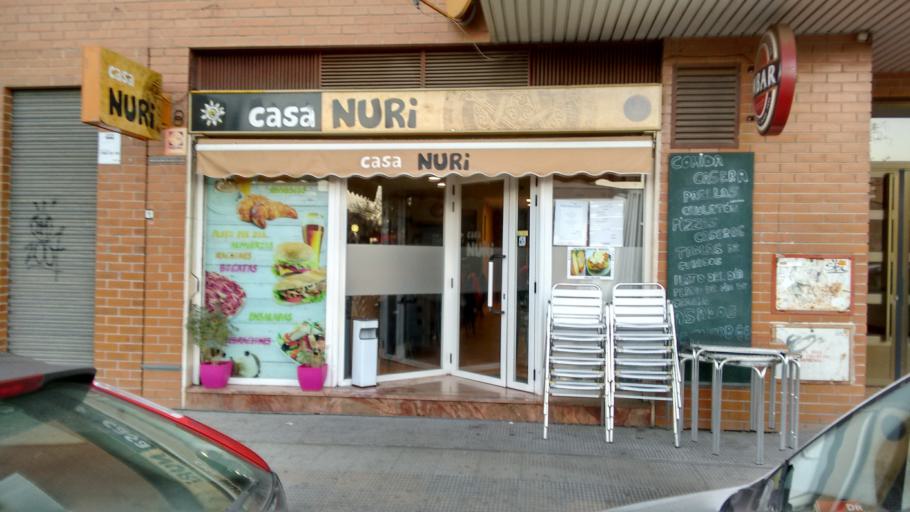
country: ES
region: Aragon
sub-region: Provincia de Zaragoza
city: Zaragoza
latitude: 41.6725
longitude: -0.8755
